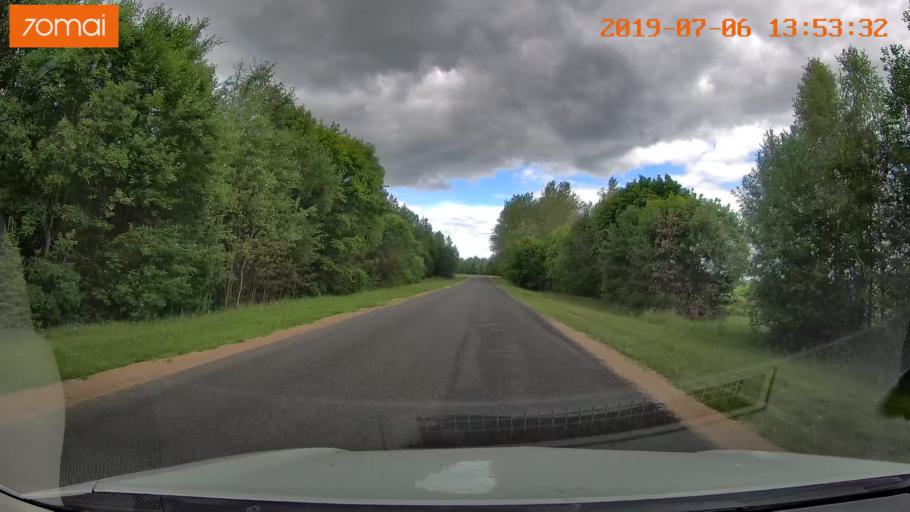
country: BY
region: Minsk
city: Ivyanyets
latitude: 53.7352
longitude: 26.8249
